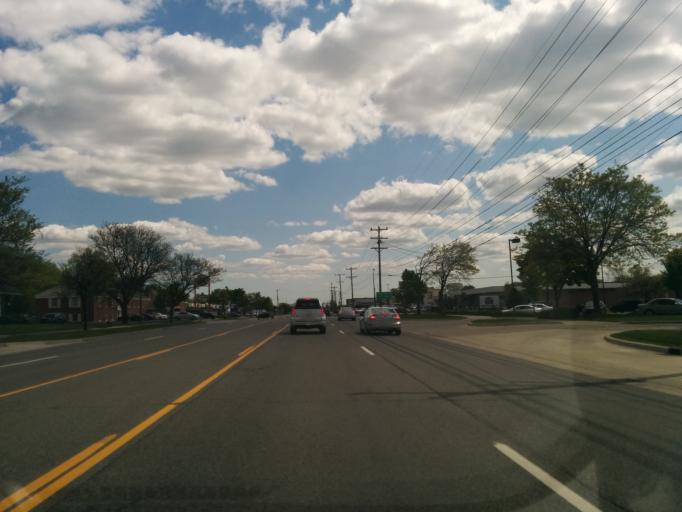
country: US
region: Michigan
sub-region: Oakland County
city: Farmington Hills
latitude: 42.5170
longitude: -83.3596
